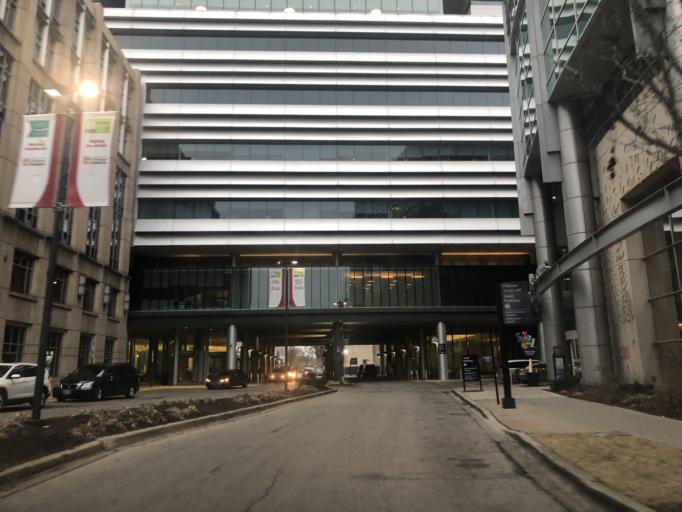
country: US
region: Illinois
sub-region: Cook County
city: Chicago
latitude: 41.7899
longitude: -87.6050
